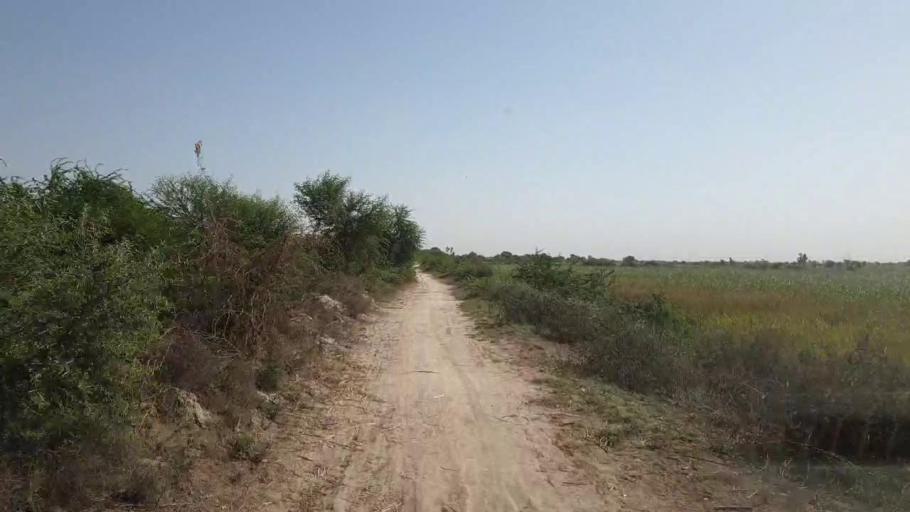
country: PK
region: Sindh
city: Kadhan
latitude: 24.6060
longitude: 69.0021
